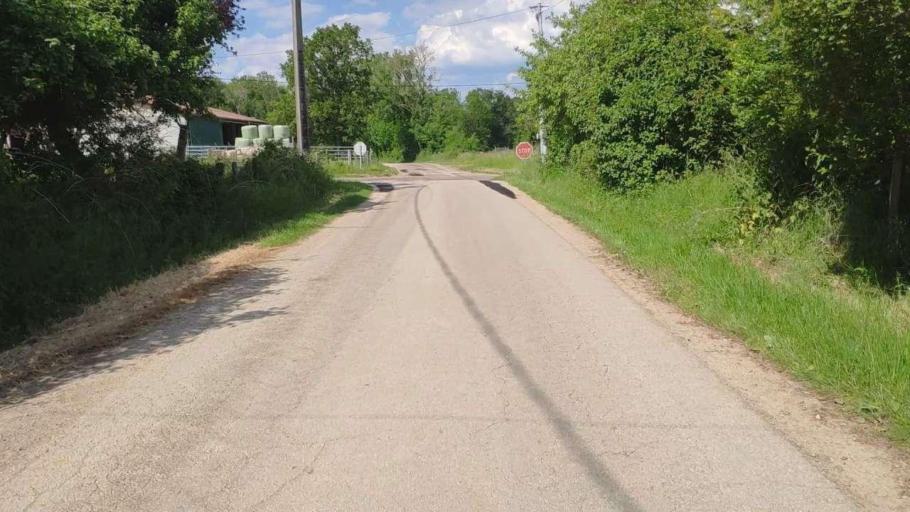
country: FR
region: Franche-Comte
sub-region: Departement du Jura
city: Bletterans
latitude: 46.8294
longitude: 5.4086
